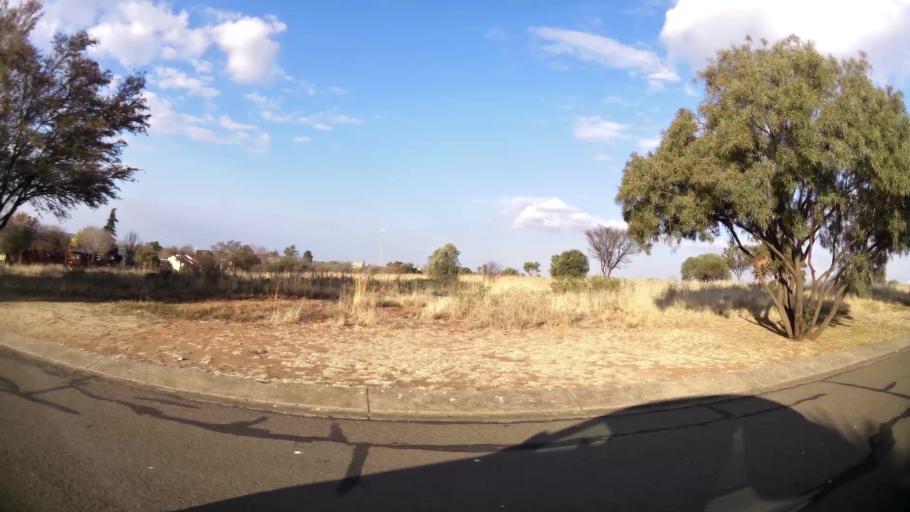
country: ZA
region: Orange Free State
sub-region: Mangaung Metropolitan Municipality
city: Bloemfontein
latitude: -29.1502
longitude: 26.1807
